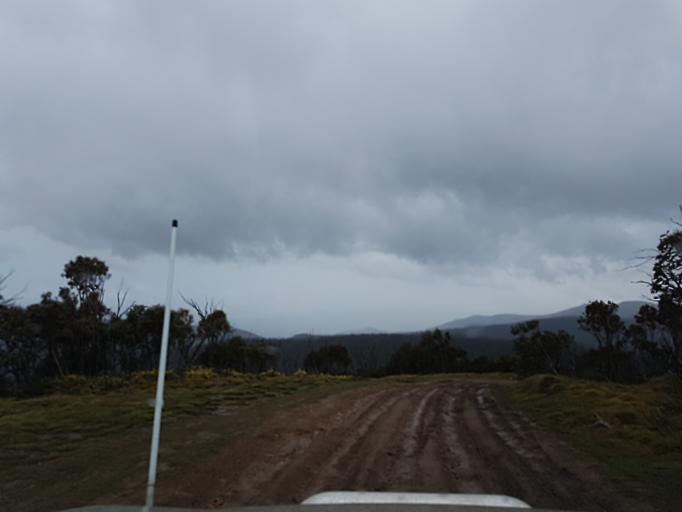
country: AU
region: Victoria
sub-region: Alpine
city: Mount Beauty
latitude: -37.0859
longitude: 147.1144
